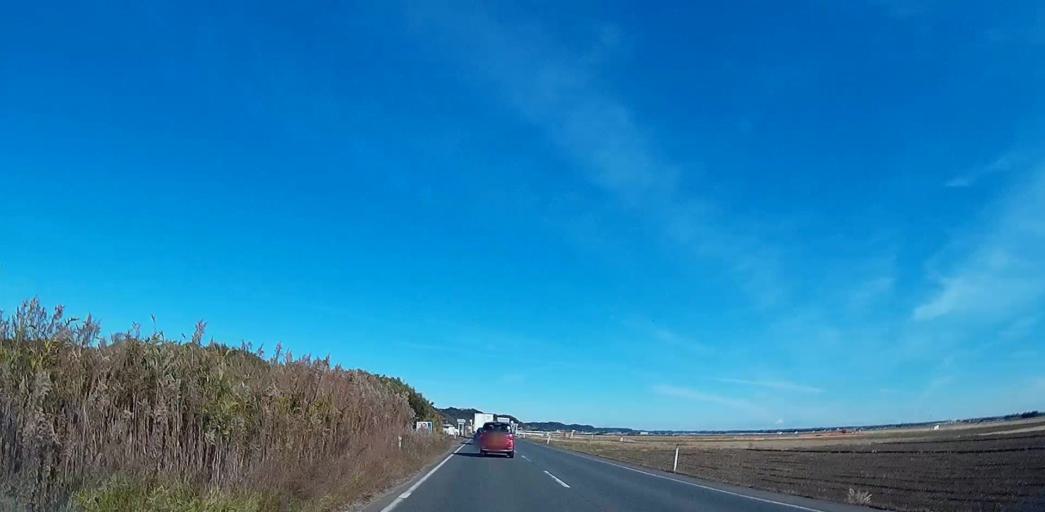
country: JP
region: Chiba
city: Yokaichiba
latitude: 35.7431
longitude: 140.5655
